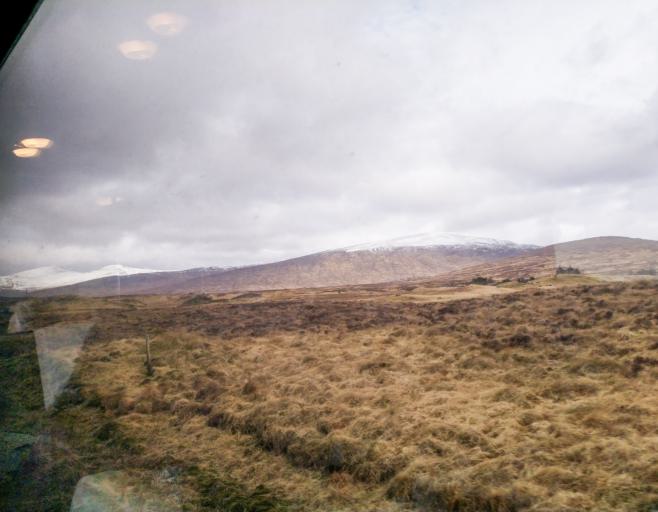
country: GB
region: Scotland
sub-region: Highland
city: Spean Bridge
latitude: 56.7393
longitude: -4.6627
